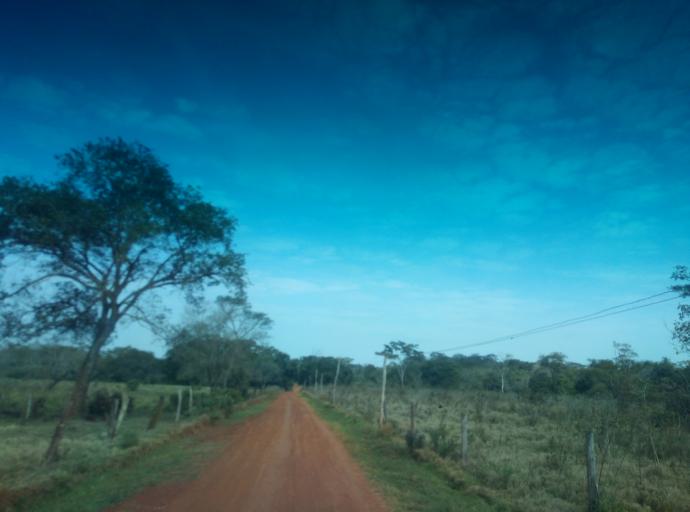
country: PY
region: Caaguazu
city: Carayao
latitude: -25.1988
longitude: -56.2529
